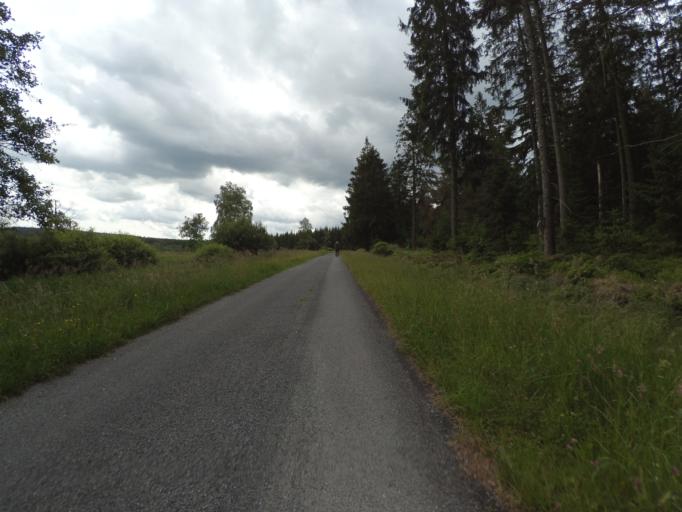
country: DE
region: North Rhine-Westphalia
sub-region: Regierungsbezirk Koln
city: Monschau
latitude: 50.5832
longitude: 6.1797
